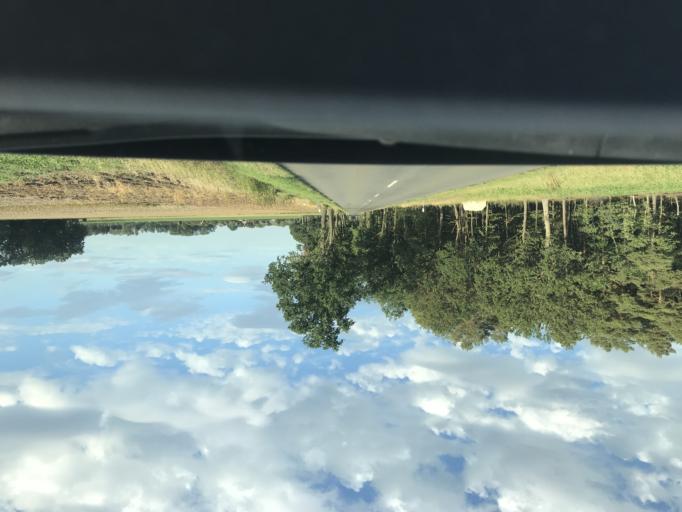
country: DE
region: Lower Saxony
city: Stadensen
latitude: 52.8827
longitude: 10.5378
